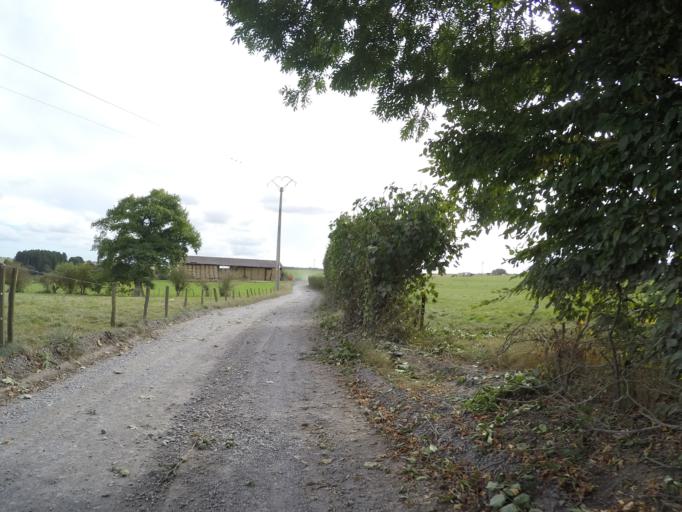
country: BE
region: Wallonia
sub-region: Province de Namur
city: Assesse
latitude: 50.3138
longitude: 4.9787
